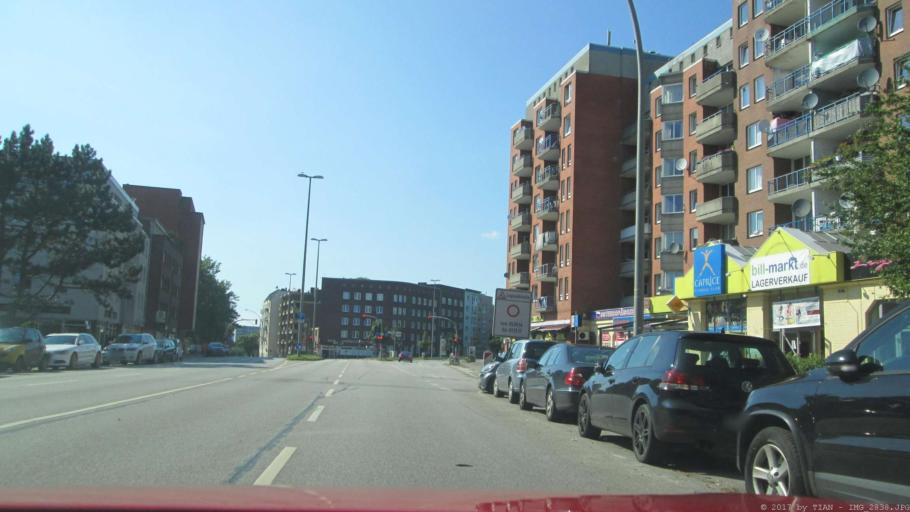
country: DE
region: Hamburg
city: Wandsbek
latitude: 53.5419
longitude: 10.0975
